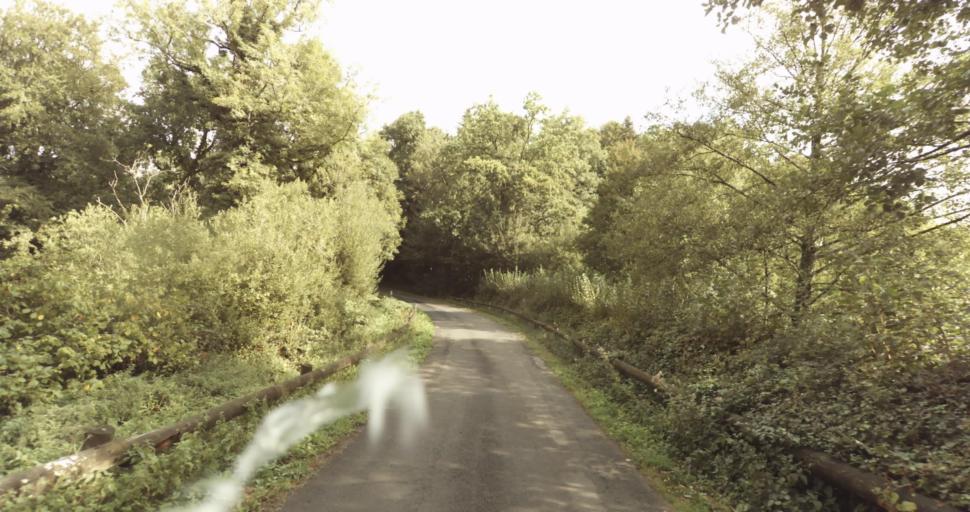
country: FR
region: Lower Normandy
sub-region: Departement de l'Orne
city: Gace
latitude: 48.8435
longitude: 0.3238
